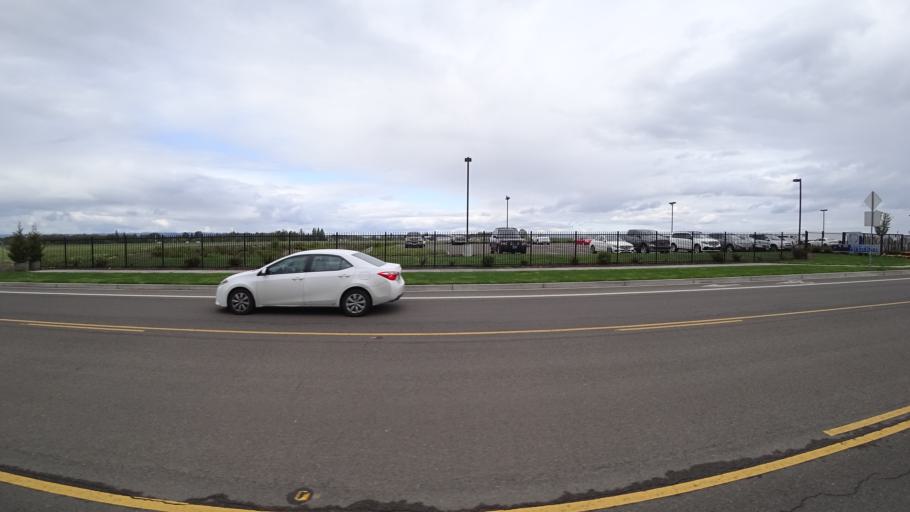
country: US
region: Oregon
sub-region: Washington County
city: Hillsboro
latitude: 45.5443
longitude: -122.9579
